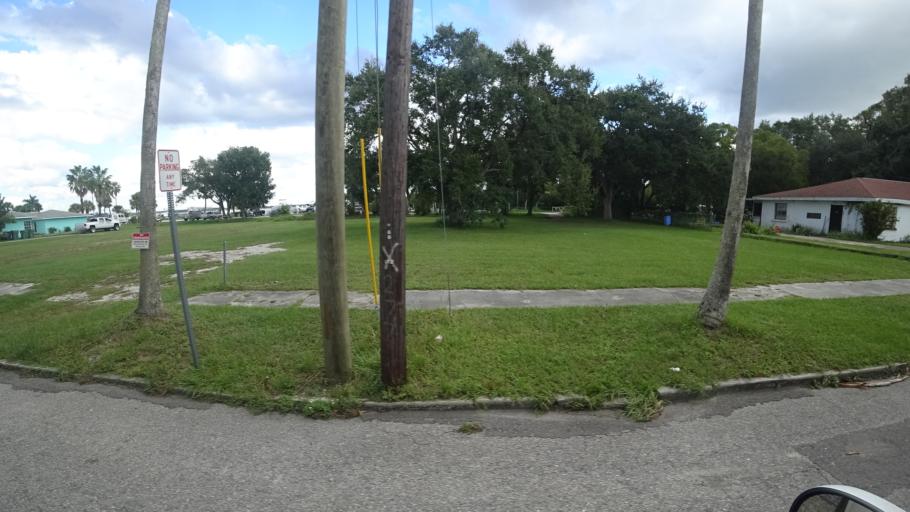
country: US
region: Florida
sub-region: Manatee County
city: Bradenton
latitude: 27.4986
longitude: -82.5576
